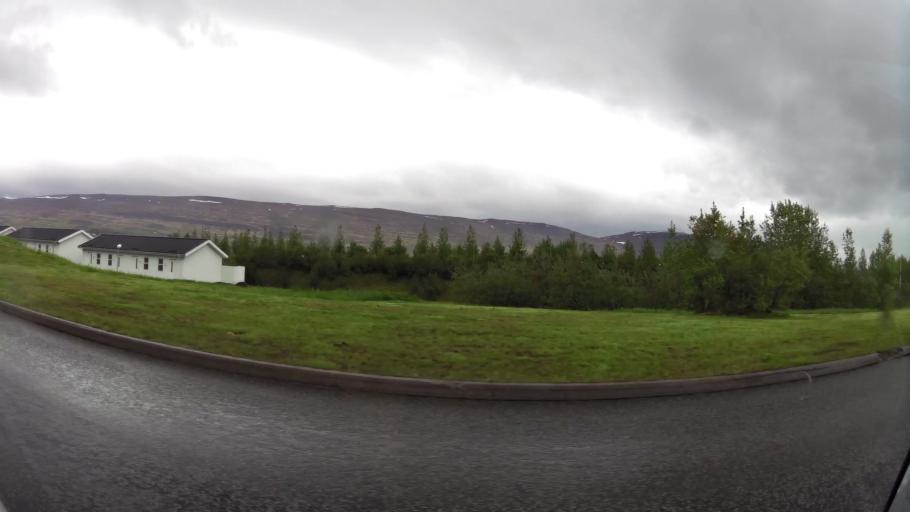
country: IS
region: Northeast
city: Akureyri
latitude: 65.6689
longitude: -18.0956
